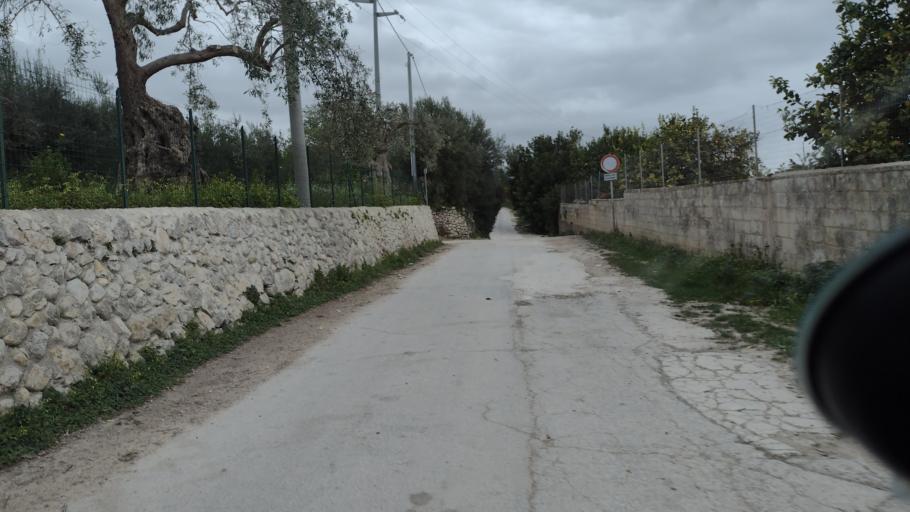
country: IT
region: Sicily
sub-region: Provincia di Siracusa
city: Avola
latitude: 36.9029
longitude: 15.1109
